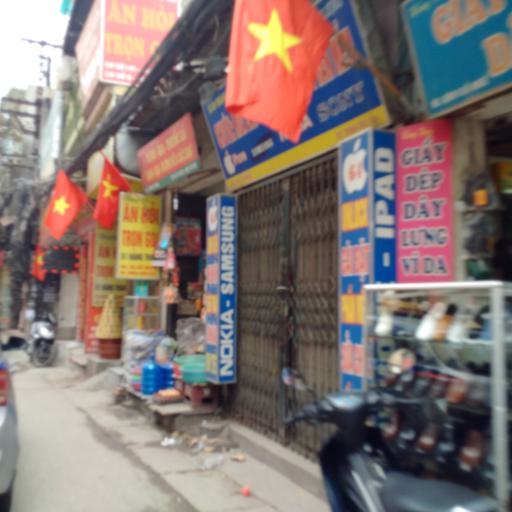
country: VN
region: Ha Noi
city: Cau Dien
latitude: 21.0600
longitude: 105.7825
